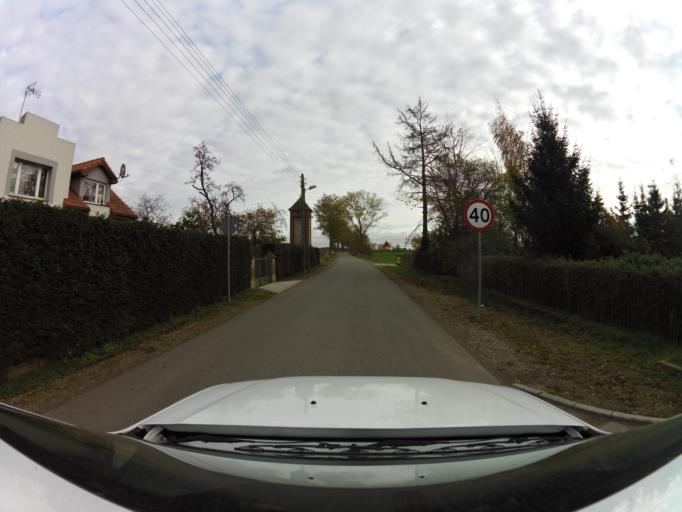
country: PL
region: West Pomeranian Voivodeship
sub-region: Powiat gryficki
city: Cerkwica
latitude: 54.0491
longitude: 15.1076
